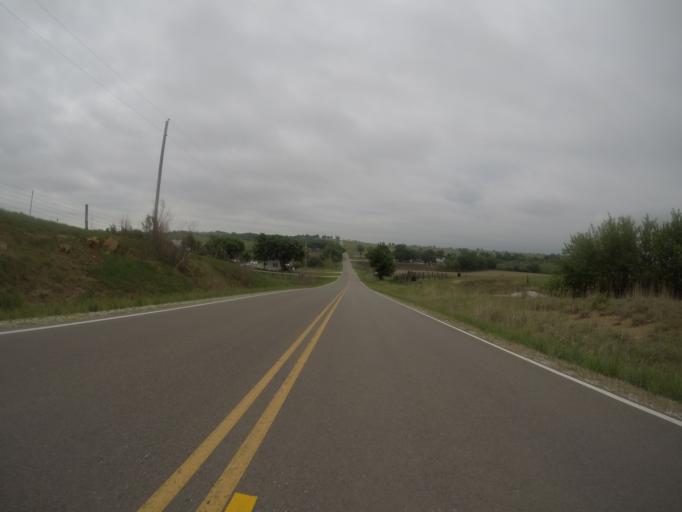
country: US
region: Kansas
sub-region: Pottawatomie County
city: Westmoreland
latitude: 39.5078
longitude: -96.1918
